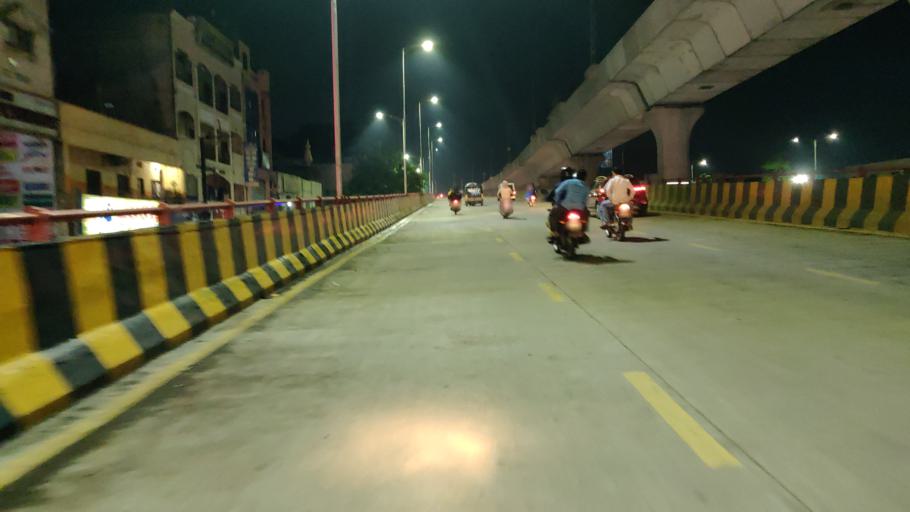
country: IN
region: Telangana
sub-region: Rangareddi
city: Lal Bahadur Nagar
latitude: 17.3486
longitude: 78.5491
